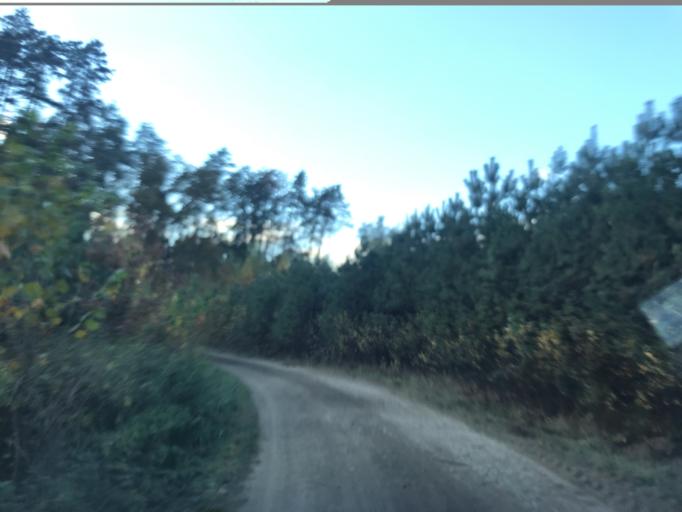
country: PL
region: Warmian-Masurian Voivodeship
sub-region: Powiat dzialdowski
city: Lidzbark
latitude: 53.2313
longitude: 19.7919
